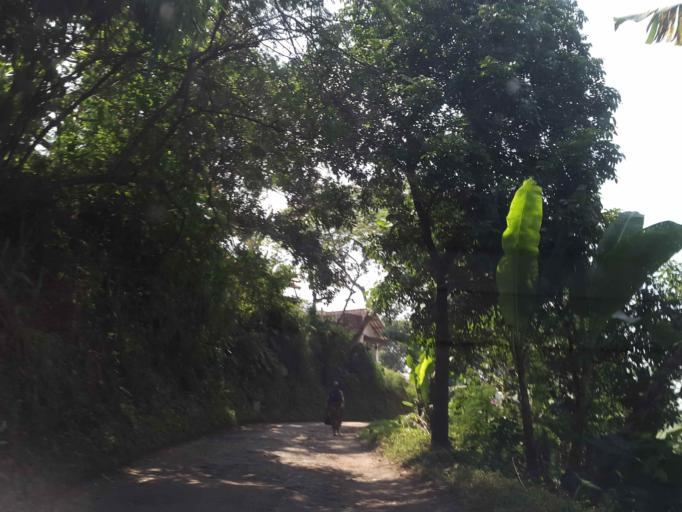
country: ID
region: West Java
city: Sukabumi
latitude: -6.8041
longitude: 107.0596
